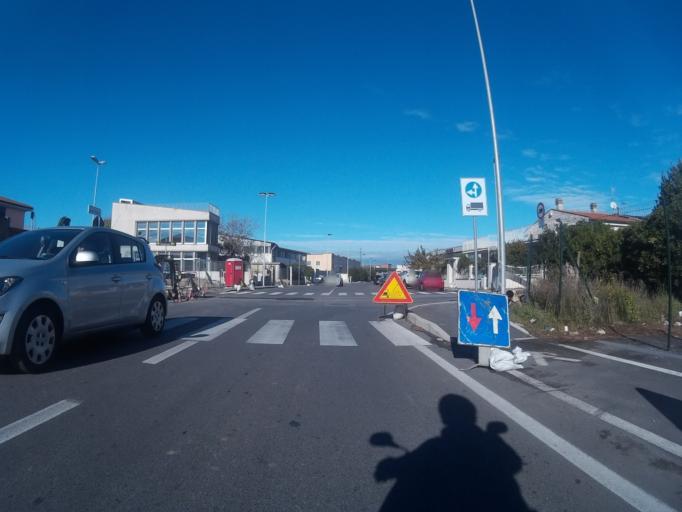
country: IT
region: Tuscany
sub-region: Provincia di Livorno
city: Livorno
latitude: 43.5649
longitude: 10.3369
